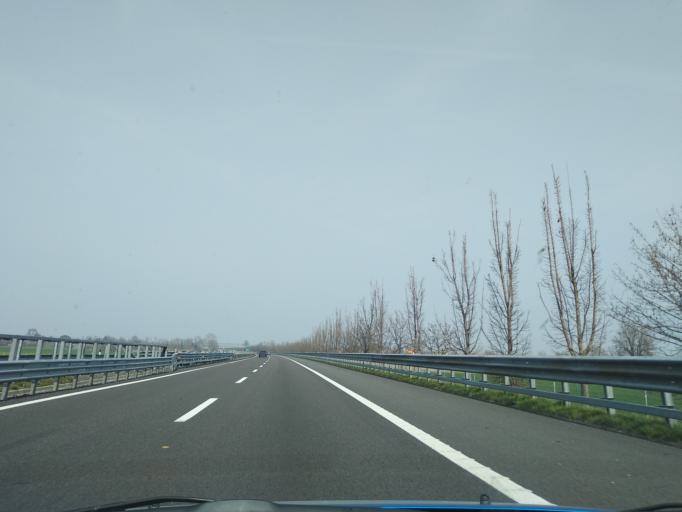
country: IT
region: Veneto
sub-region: Provincia di Vicenza
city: Vigardolo
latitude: 45.6038
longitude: 11.6002
